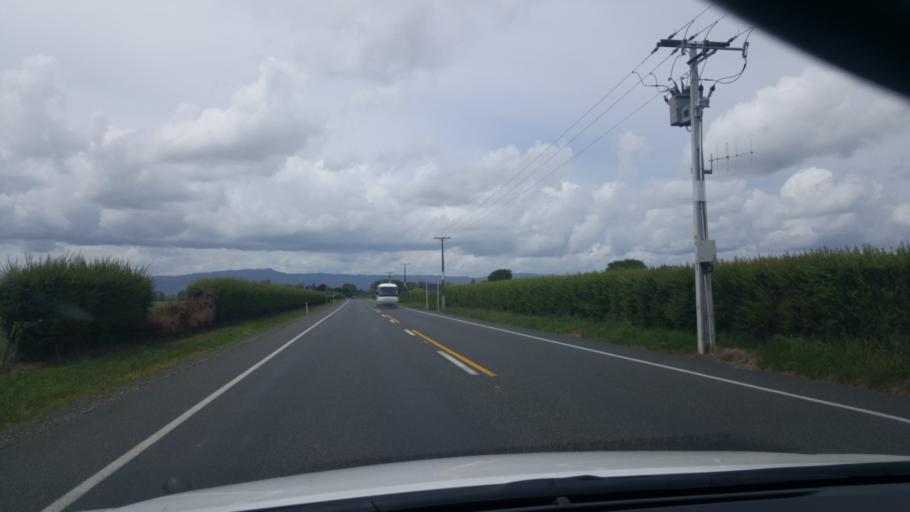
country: NZ
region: Waikato
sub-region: Matamata-Piako District
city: Matamata
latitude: -37.8829
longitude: 175.7353
